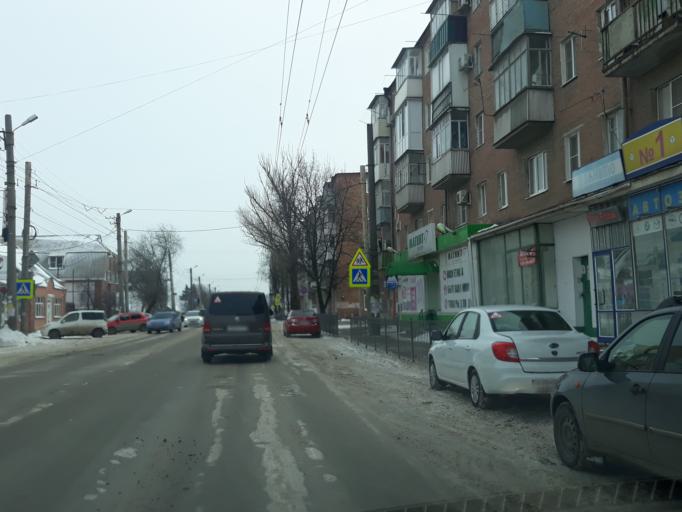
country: RU
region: Rostov
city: Taganrog
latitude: 47.2217
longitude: 38.8874
